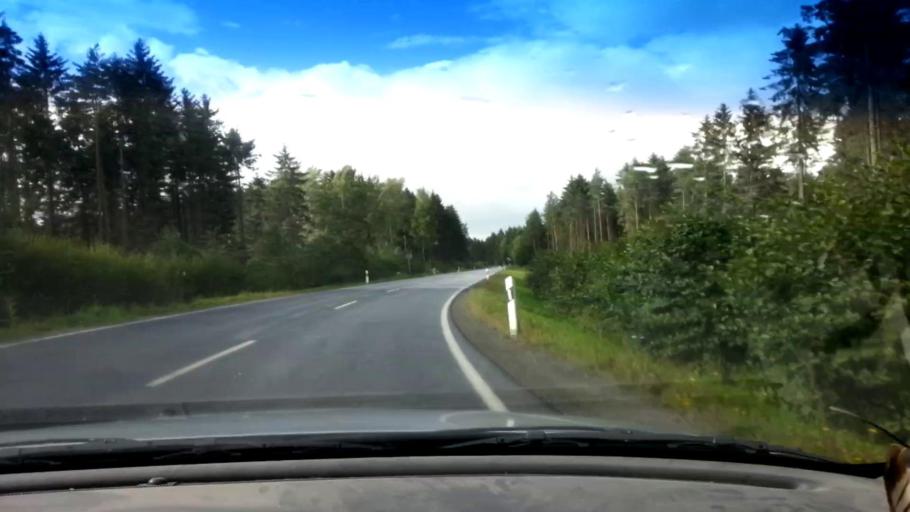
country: DE
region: Bavaria
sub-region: Upper Palatinate
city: Pechbrunn
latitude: 49.9934
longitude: 12.2083
